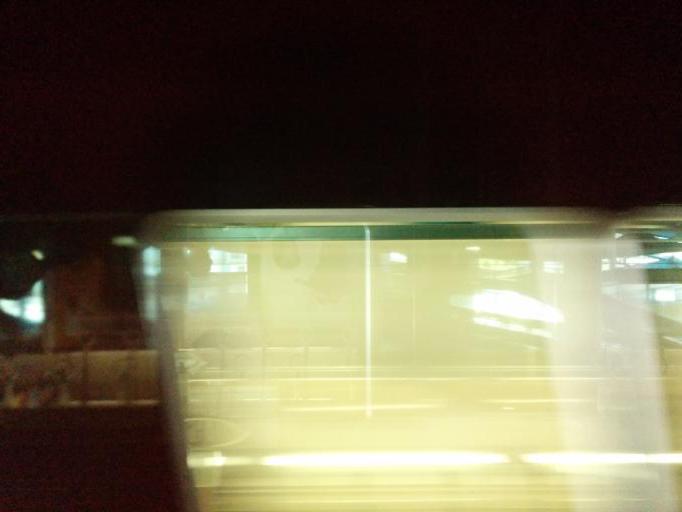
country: JP
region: Osaka
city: Ibaraki
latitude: 34.8029
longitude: 135.5655
